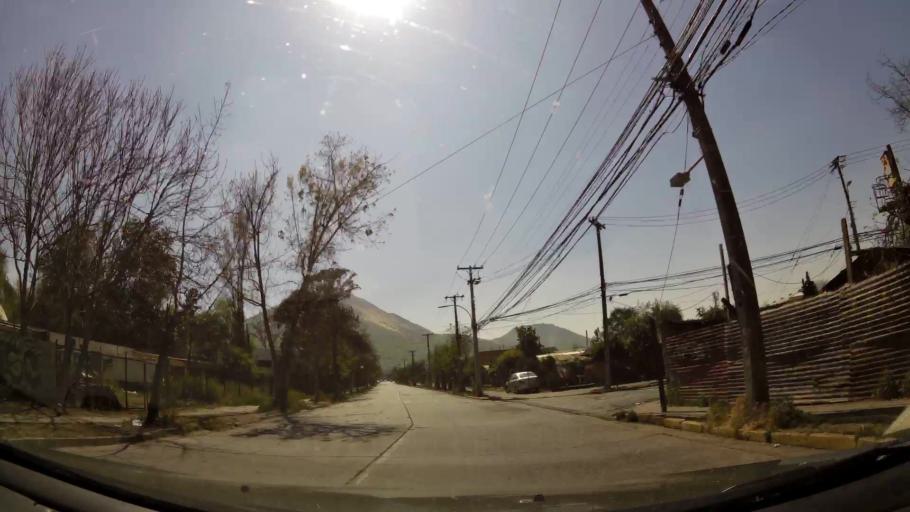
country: CL
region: Santiago Metropolitan
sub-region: Provincia de Santiago
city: Lo Prado
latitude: -33.4054
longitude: -70.7002
